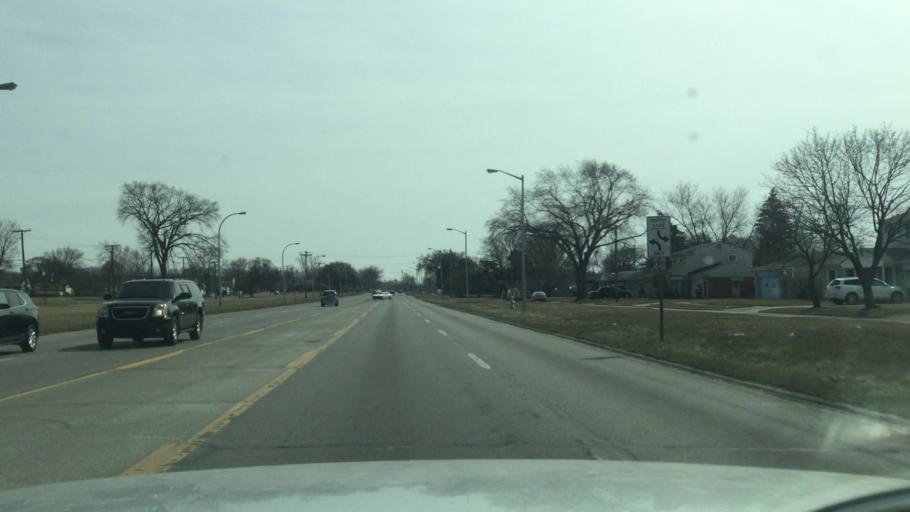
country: US
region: Michigan
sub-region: Wayne County
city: Inkster
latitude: 42.2793
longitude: -83.3289
